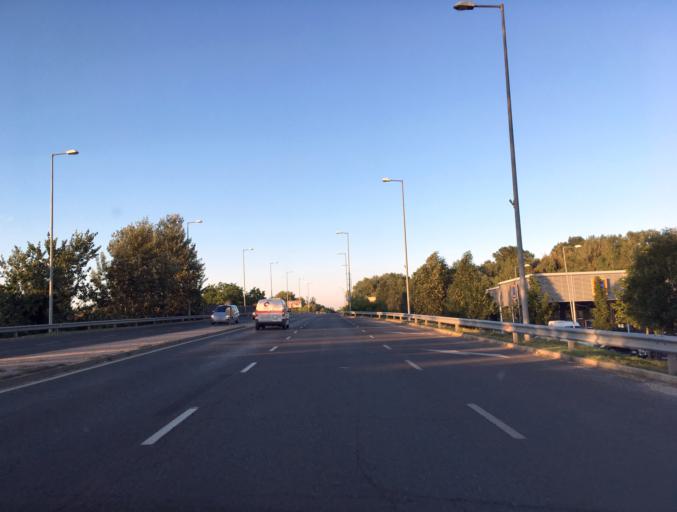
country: HU
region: Gyor-Moson-Sopron
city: Gyor
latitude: 47.6777
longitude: 17.6164
